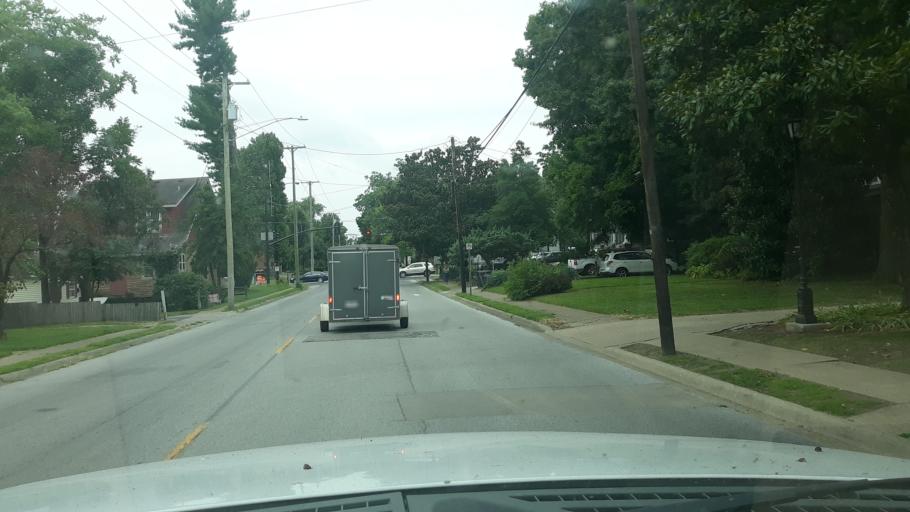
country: US
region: Illinois
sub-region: Jackson County
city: Carbondale
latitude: 37.7257
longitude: -89.2220
